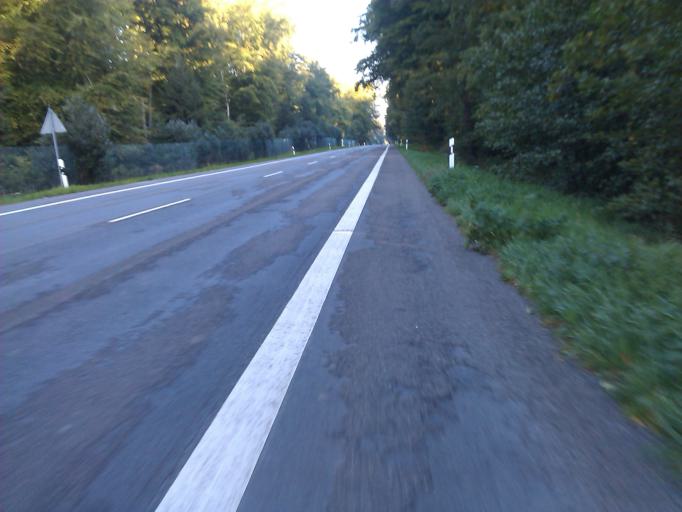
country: DE
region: Hesse
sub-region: Regierungsbezirk Darmstadt
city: Erzhausen
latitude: 49.9781
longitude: 8.6448
